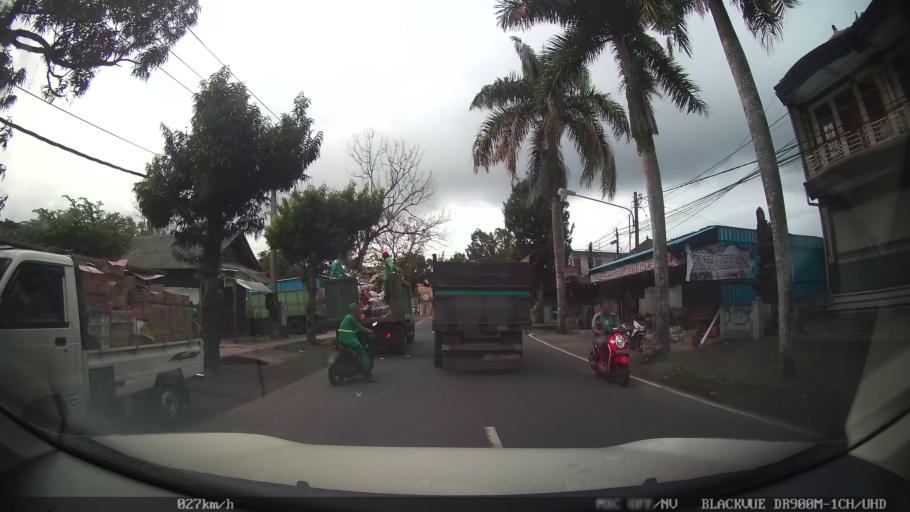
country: ID
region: Bali
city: Banjar Kelodan
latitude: -8.5365
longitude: 115.3359
